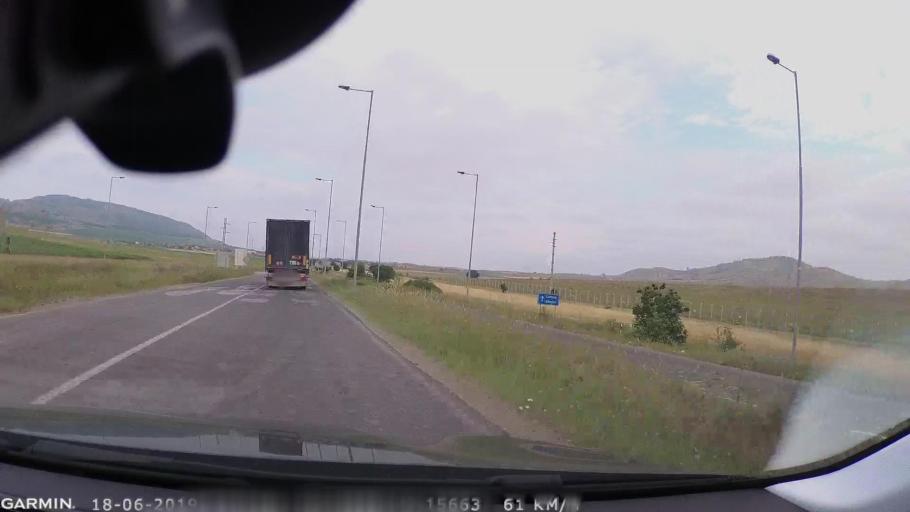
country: MK
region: Stip
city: Shtip
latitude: 41.7663
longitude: 22.1558
